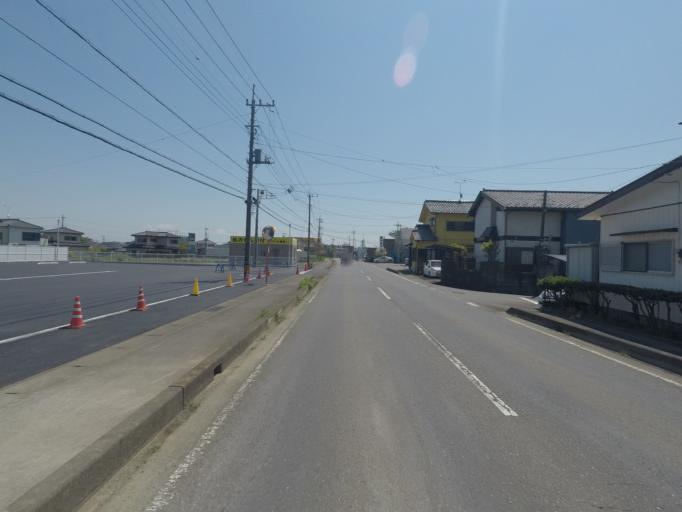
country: JP
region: Ibaraki
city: Ushiku
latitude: 35.9627
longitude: 140.1020
